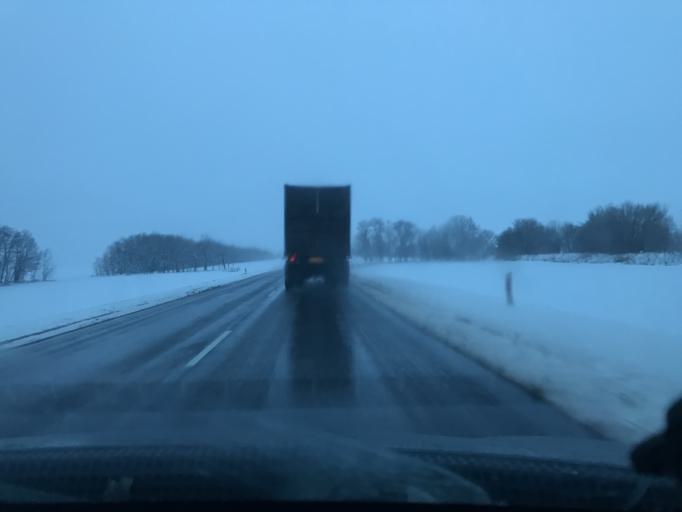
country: RU
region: Rostov
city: Letnik
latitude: 46.0348
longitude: 41.2111
